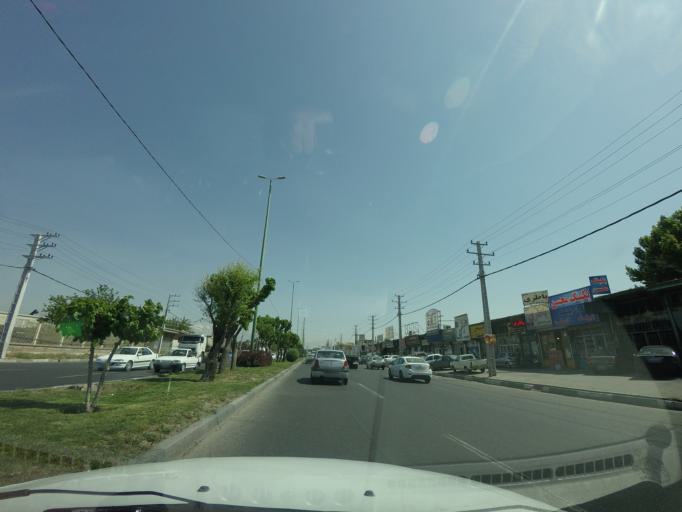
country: IR
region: Tehran
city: Eslamshahr
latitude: 35.5971
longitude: 51.2967
